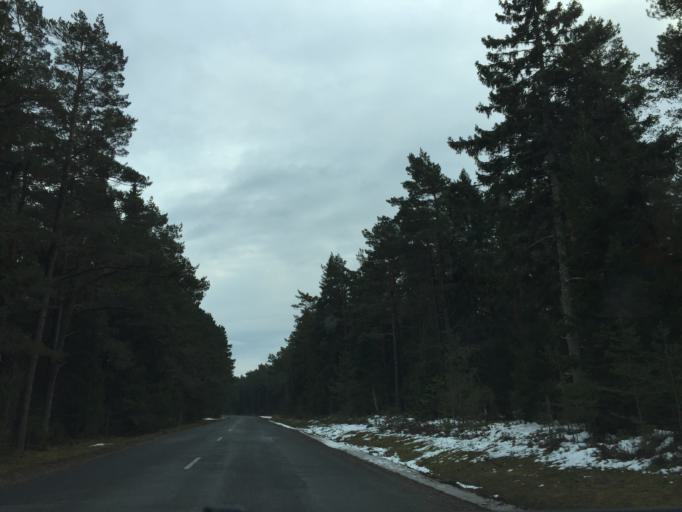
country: EE
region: Saare
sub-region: Kuressaare linn
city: Kuressaare
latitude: 58.4402
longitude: 22.0589
